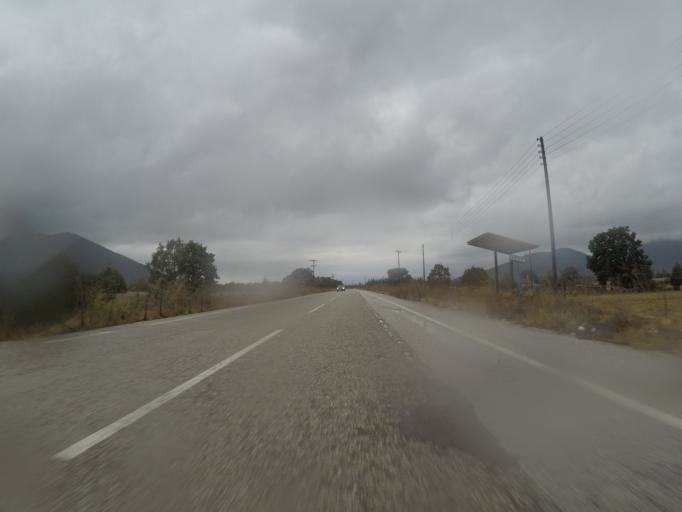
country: GR
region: Peloponnese
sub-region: Nomos Arkadias
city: Tripoli
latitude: 37.5921
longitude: 22.4286
